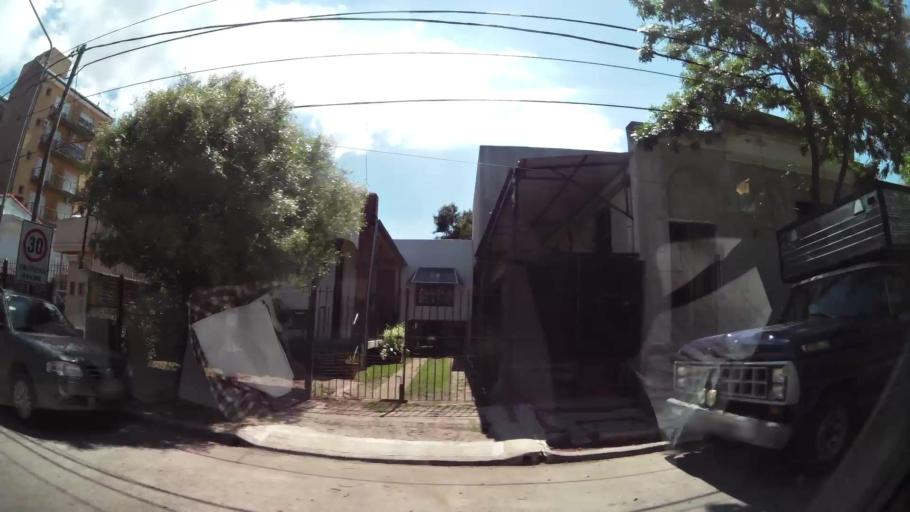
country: AR
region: Buenos Aires
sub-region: Partido de Tigre
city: Tigre
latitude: -34.4287
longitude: -58.5752
